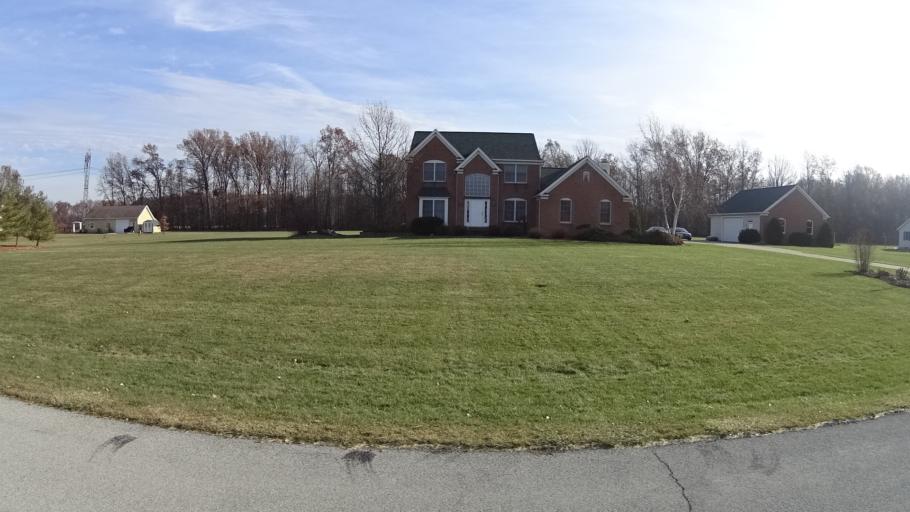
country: US
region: Ohio
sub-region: Lorain County
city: Grafton
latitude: 41.2269
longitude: -82.0348
